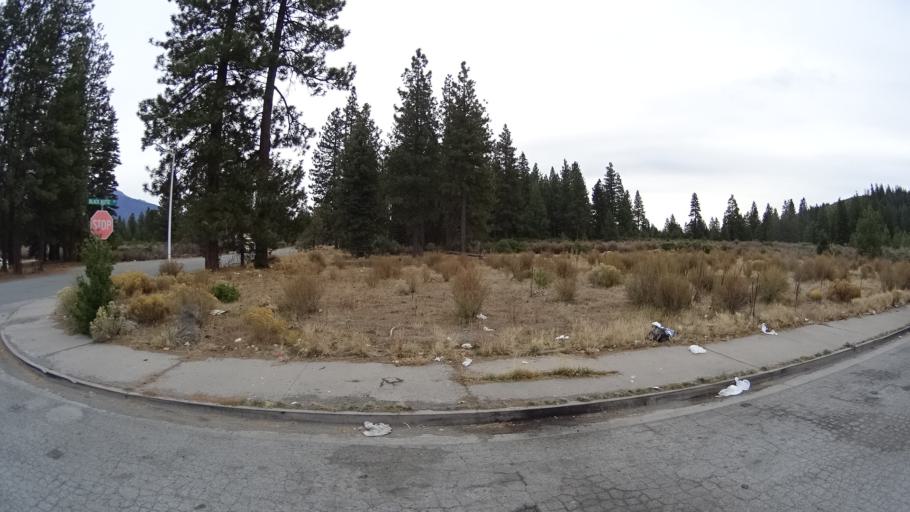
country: US
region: California
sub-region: Siskiyou County
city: Weed
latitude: 41.3969
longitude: -122.3765
